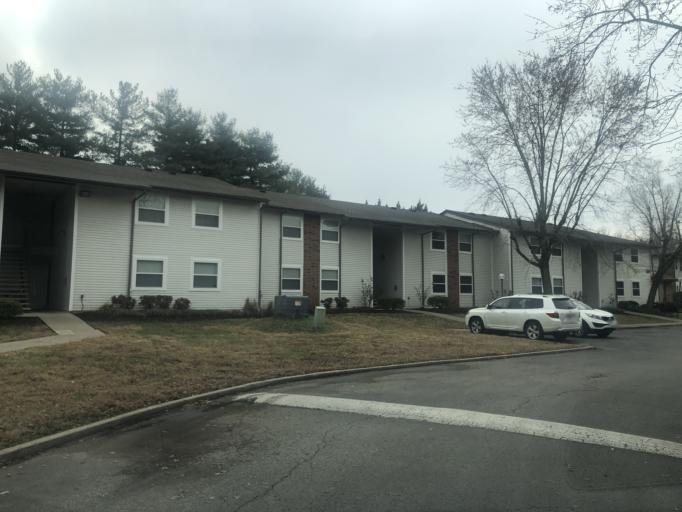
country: US
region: Tennessee
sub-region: Rutherford County
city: La Vergne
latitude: 36.0747
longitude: -86.6419
